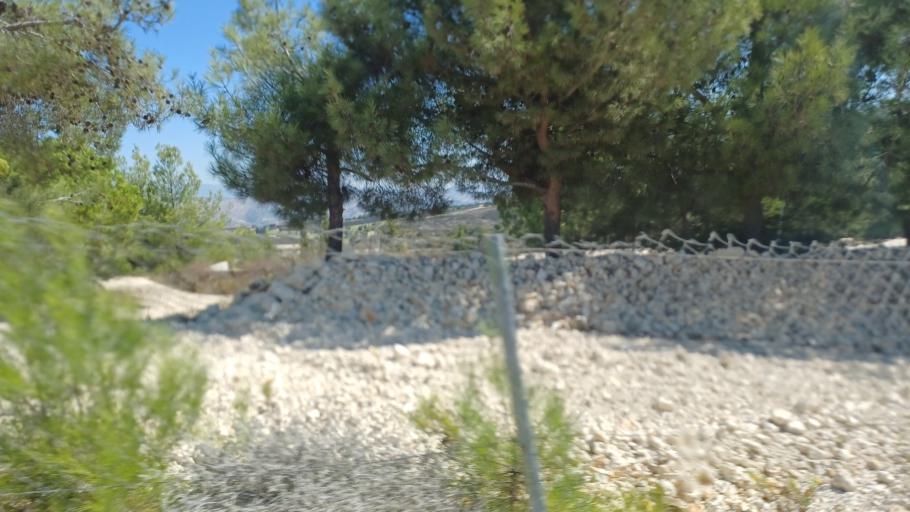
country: CY
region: Pafos
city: Mesogi
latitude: 34.8199
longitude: 32.4820
